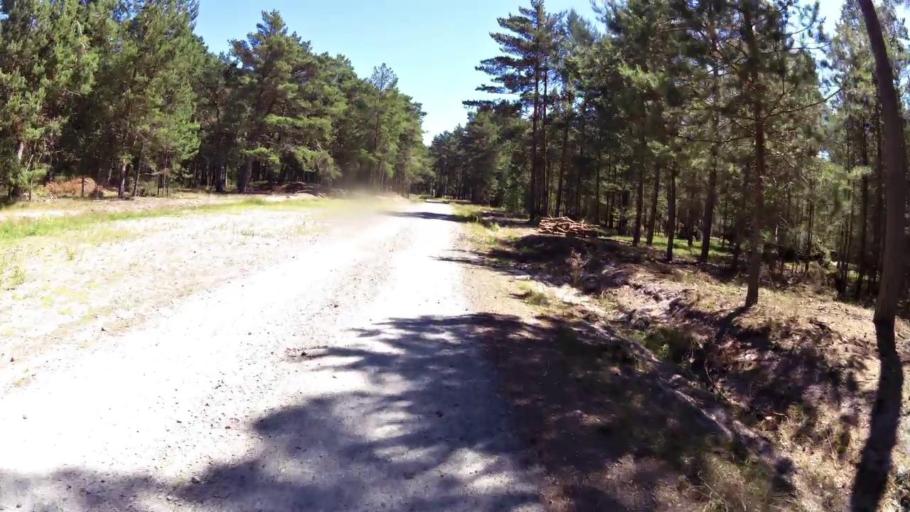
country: PL
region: West Pomeranian Voivodeship
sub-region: Powiat gryficki
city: Cerkwica
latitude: 54.0981
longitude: 15.1428
